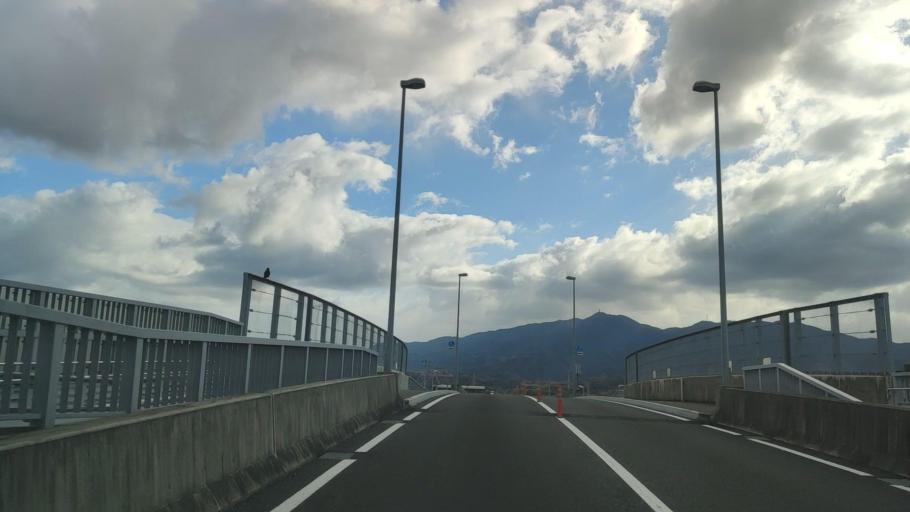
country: JP
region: Ehime
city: Hojo
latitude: 33.9716
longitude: 132.7743
